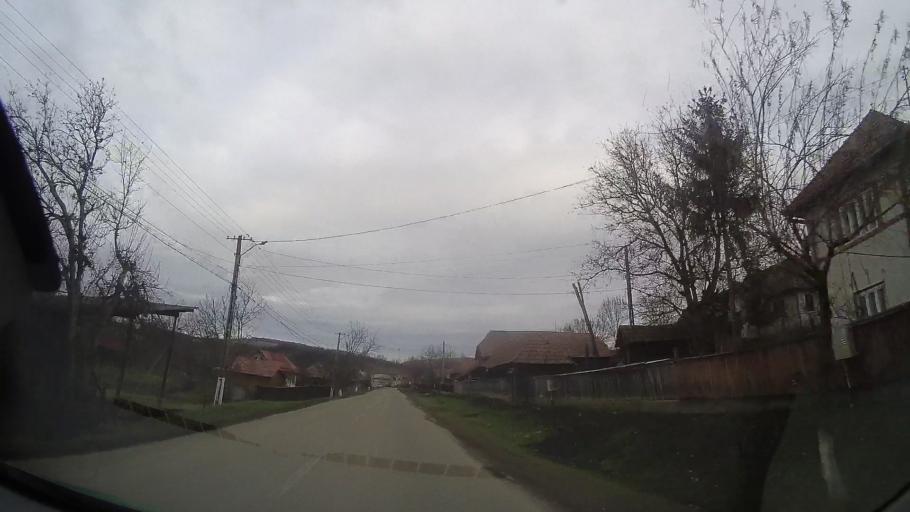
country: RO
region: Mures
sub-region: Comuna Faragau
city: Faragau
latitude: 46.7609
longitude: 24.5172
